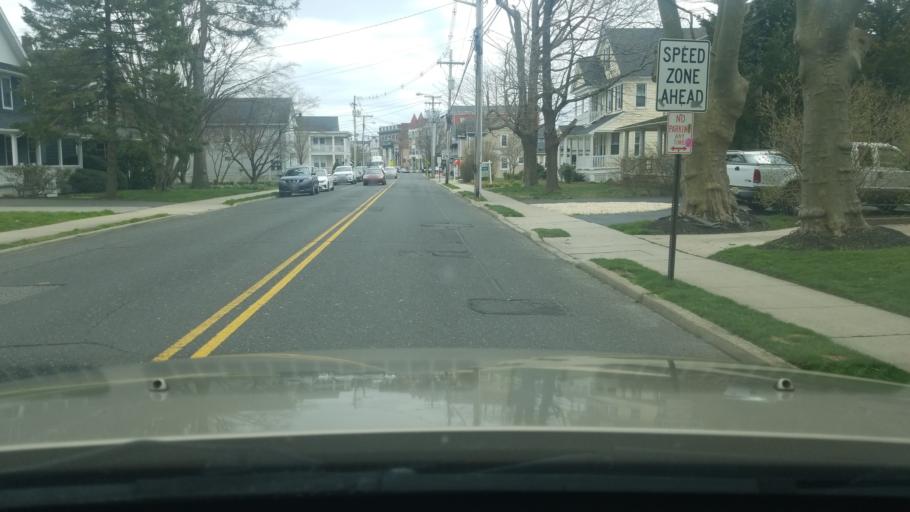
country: US
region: New Jersey
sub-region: Monmouth County
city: Manasquan
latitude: 40.1254
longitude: -74.0528
